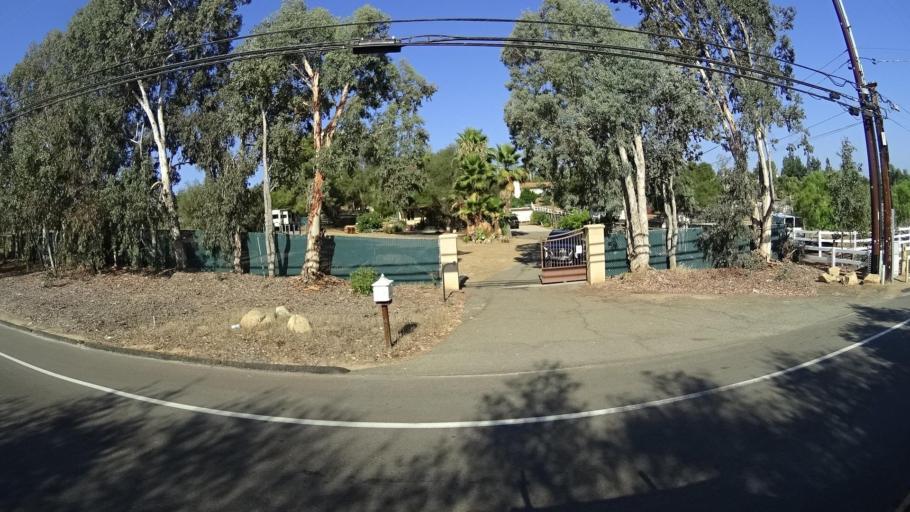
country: US
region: California
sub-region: San Diego County
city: Bonsall
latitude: 33.3264
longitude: -117.2449
